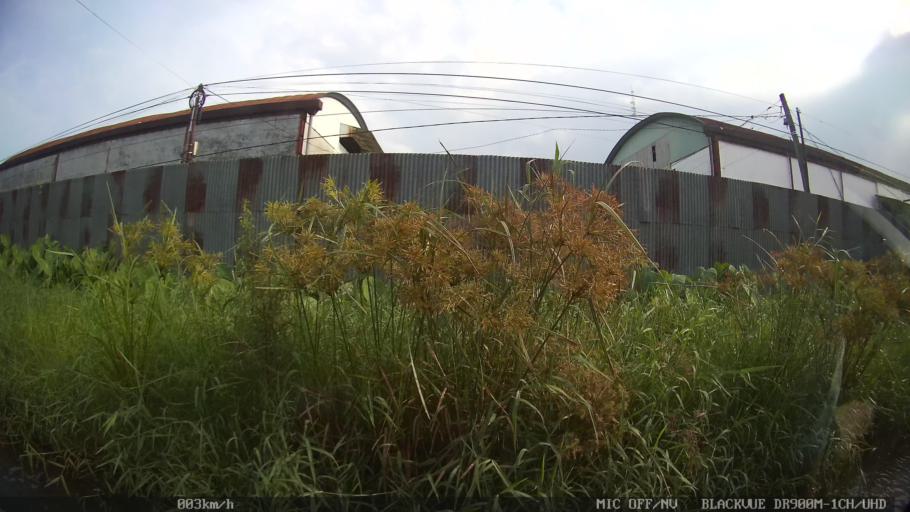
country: ID
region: North Sumatra
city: Medan
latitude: 3.6053
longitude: 98.7373
